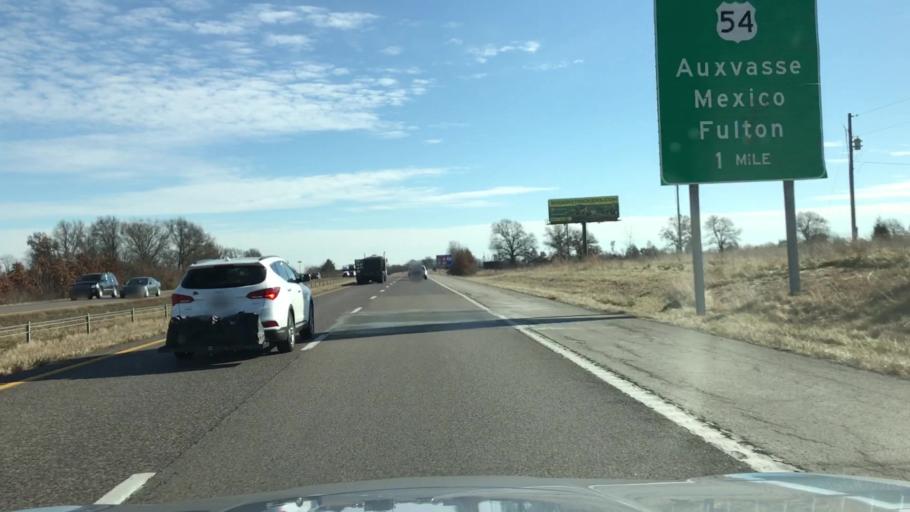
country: US
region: Missouri
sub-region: Callaway County
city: Fulton
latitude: 38.9484
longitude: -91.9589
